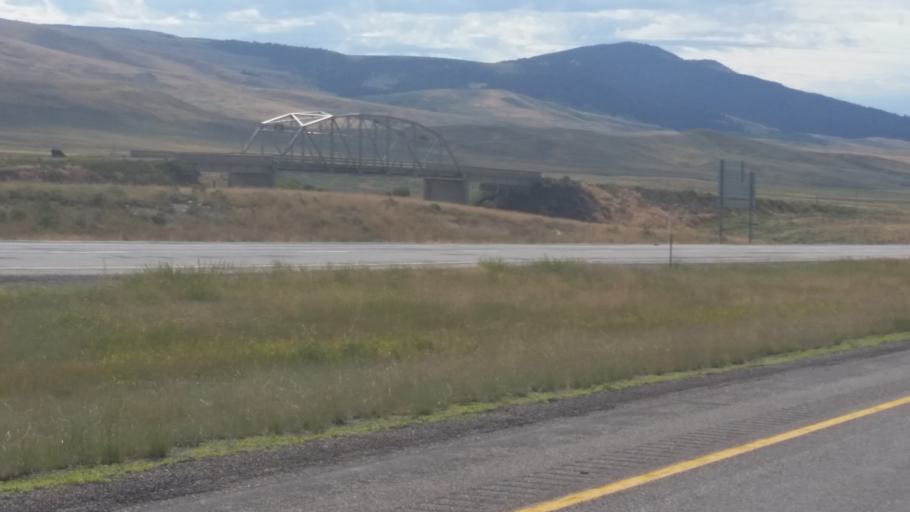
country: US
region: Idaho
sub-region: Clark County
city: Dubois
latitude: 44.5512
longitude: -112.3022
